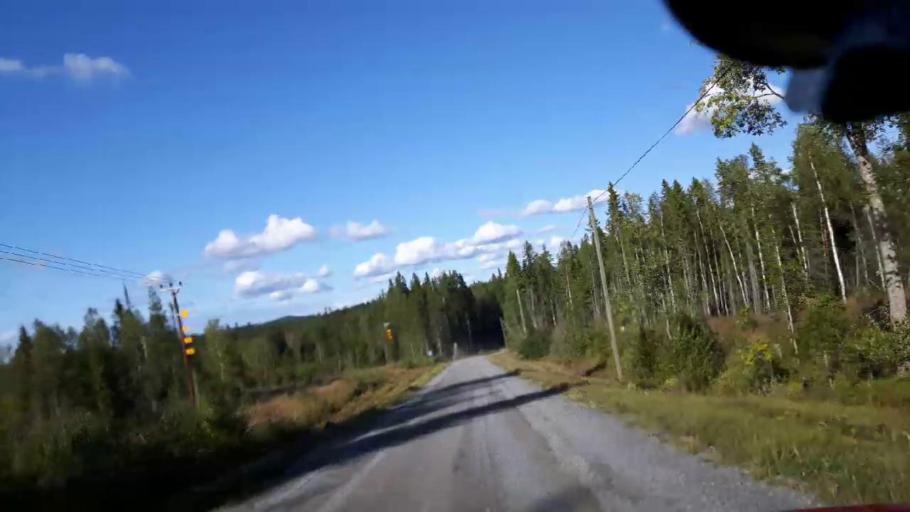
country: SE
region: Jaemtland
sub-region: Ragunda Kommun
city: Hammarstrand
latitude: 63.5123
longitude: 16.0488
